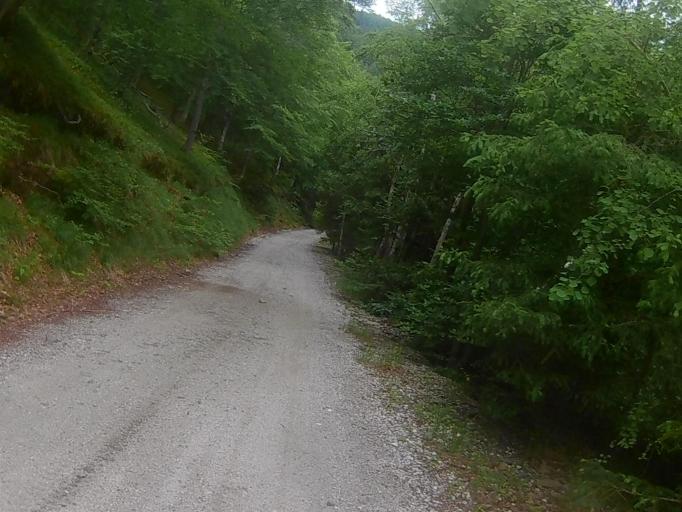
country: SI
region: Maribor
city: Limbus
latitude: 46.5204
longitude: 15.5656
